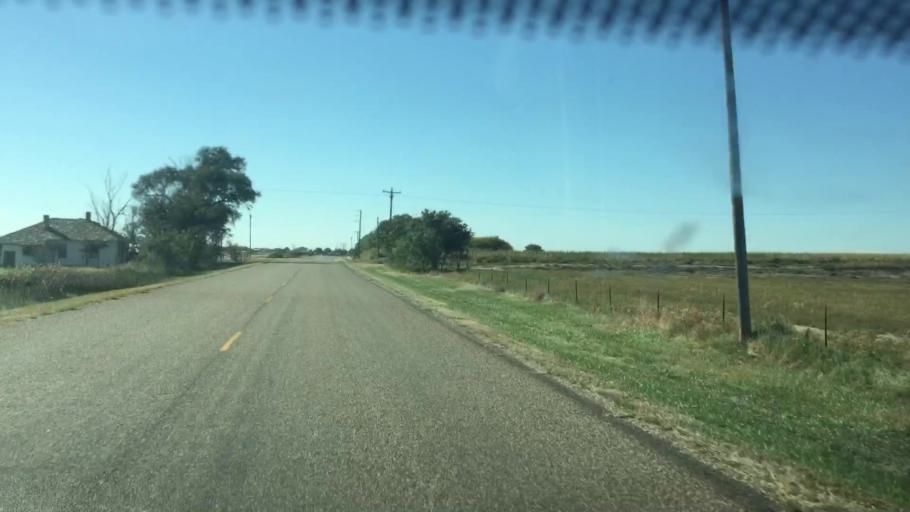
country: US
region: Colorado
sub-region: Prowers County
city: Lamar
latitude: 38.1160
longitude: -102.5929
